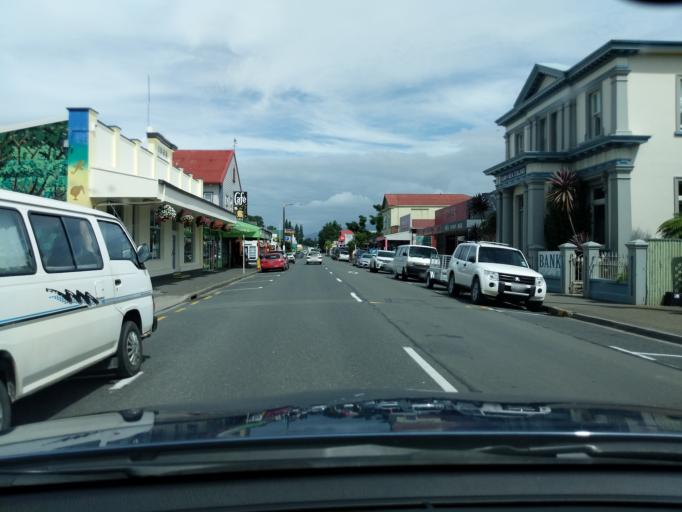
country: NZ
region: Tasman
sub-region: Tasman District
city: Takaka
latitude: -40.8582
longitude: 172.8063
